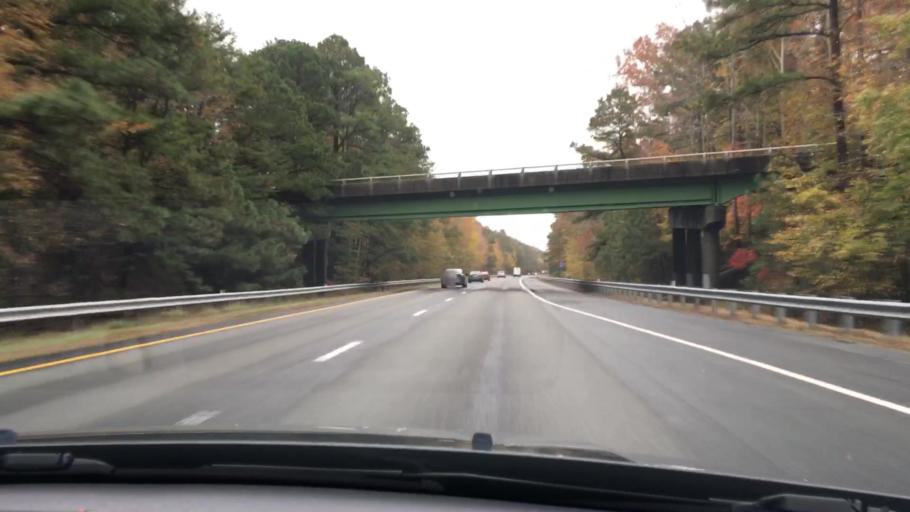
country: US
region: Virginia
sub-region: New Kent County
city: New Kent
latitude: 37.4778
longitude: -76.9188
